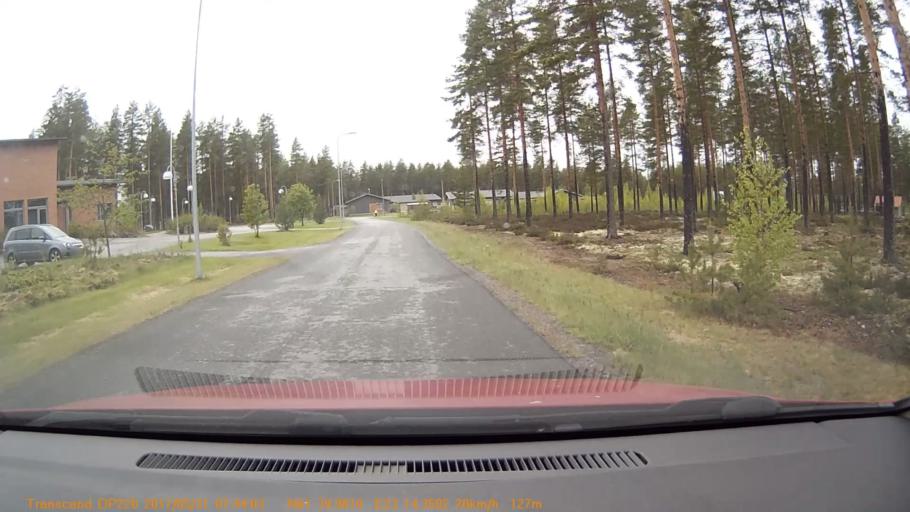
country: FI
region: Pirkanmaa
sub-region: Tampere
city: Viljakkala
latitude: 61.6665
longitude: 23.2395
